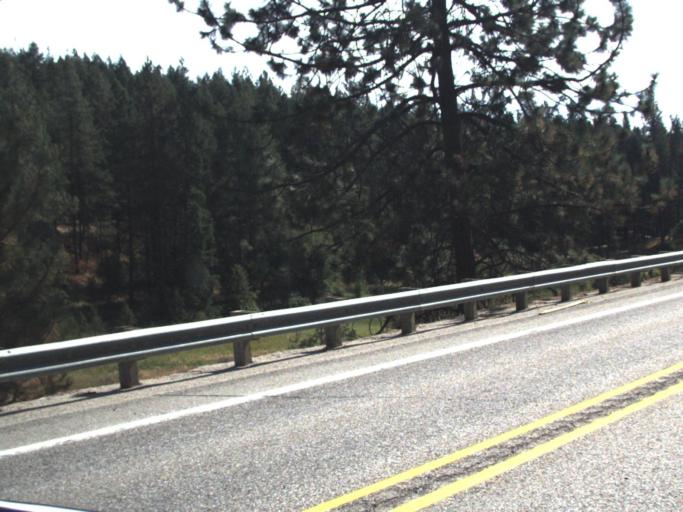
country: US
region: Washington
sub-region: Stevens County
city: Chewelah
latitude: 48.1823
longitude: -117.6999
